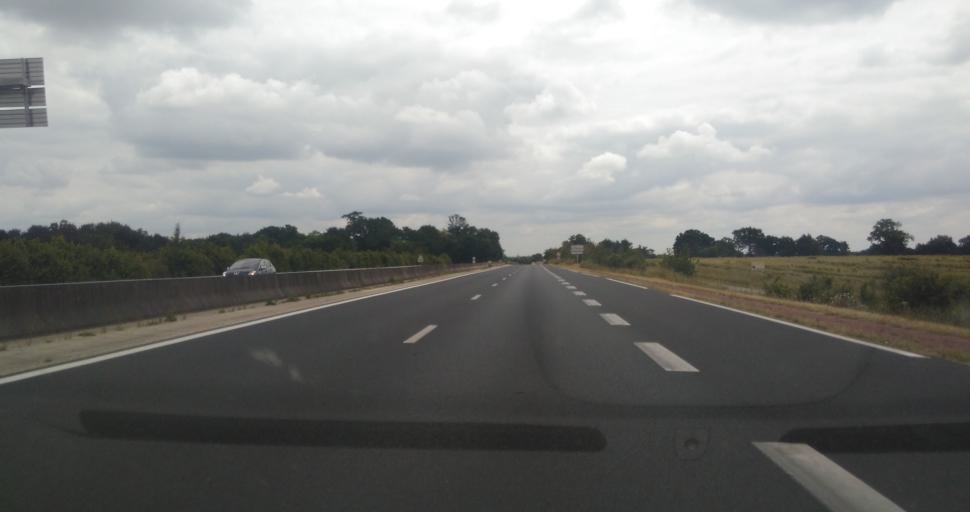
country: FR
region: Pays de la Loire
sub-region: Departement de la Vendee
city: Bournezeau
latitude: 46.6433
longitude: -1.1979
